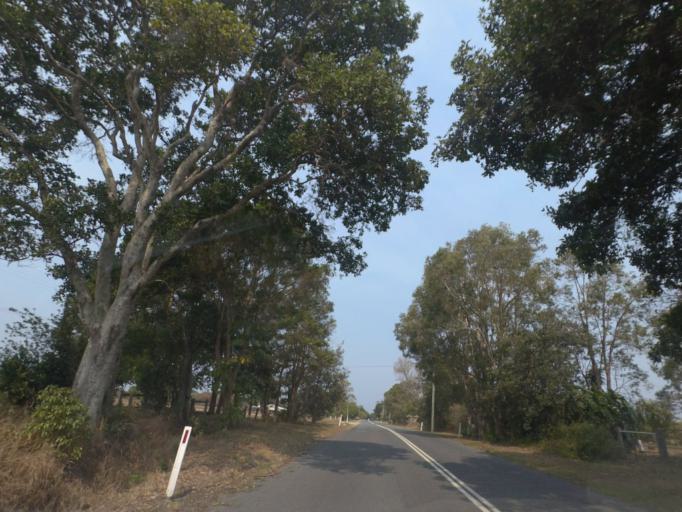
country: AU
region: New South Wales
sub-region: Tweed
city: Burringbar
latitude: -28.4554
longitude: 153.5399
